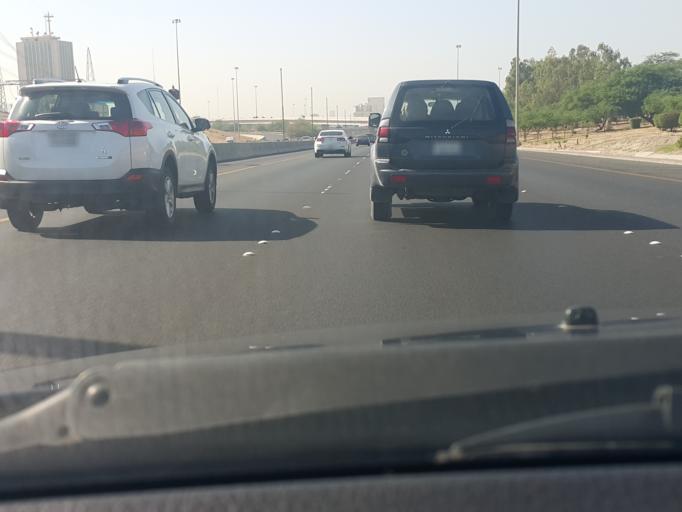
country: KW
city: Bayan
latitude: 29.3012
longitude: 48.0247
